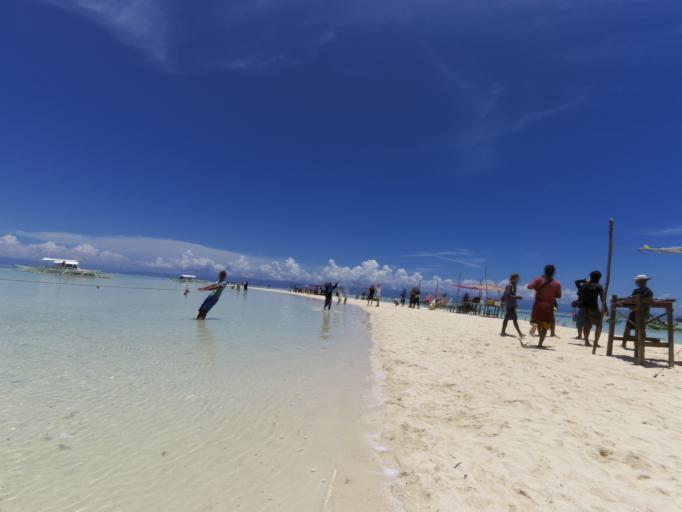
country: PH
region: Central Visayas
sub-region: Province of Bohol
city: Doljo
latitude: 9.5560
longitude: 123.7180
